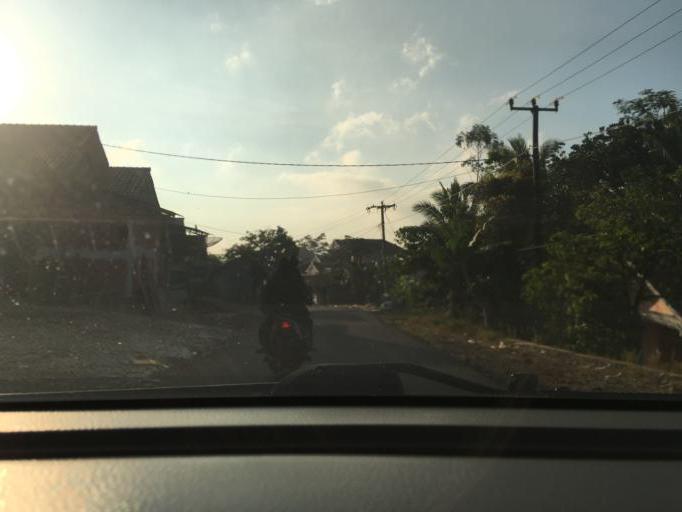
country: ID
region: West Java
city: Maniis
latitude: -7.0384
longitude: 108.3158
